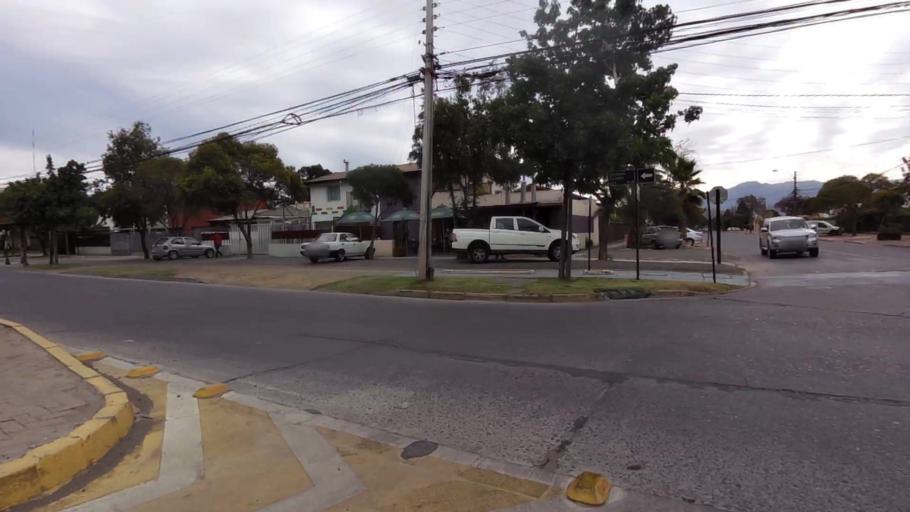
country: CL
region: O'Higgins
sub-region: Provincia de Cachapoal
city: Rancagua
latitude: -34.1611
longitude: -70.7332
